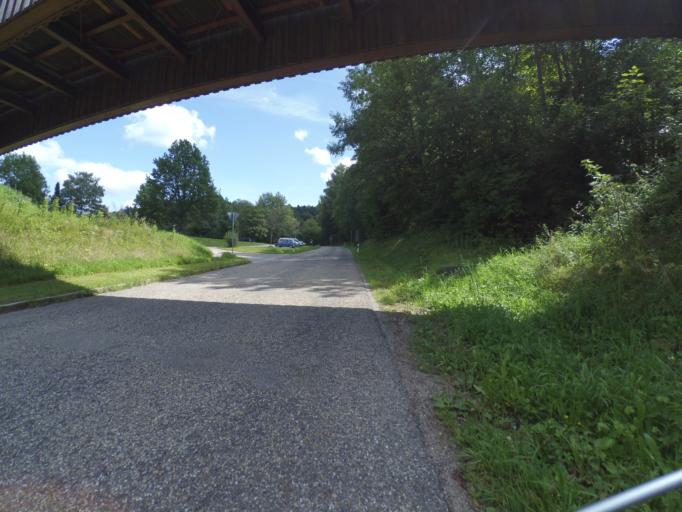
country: DE
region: Baden-Wuerttemberg
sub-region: Freiburg Region
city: Waldkirch
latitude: 48.0936
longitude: 7.9807
